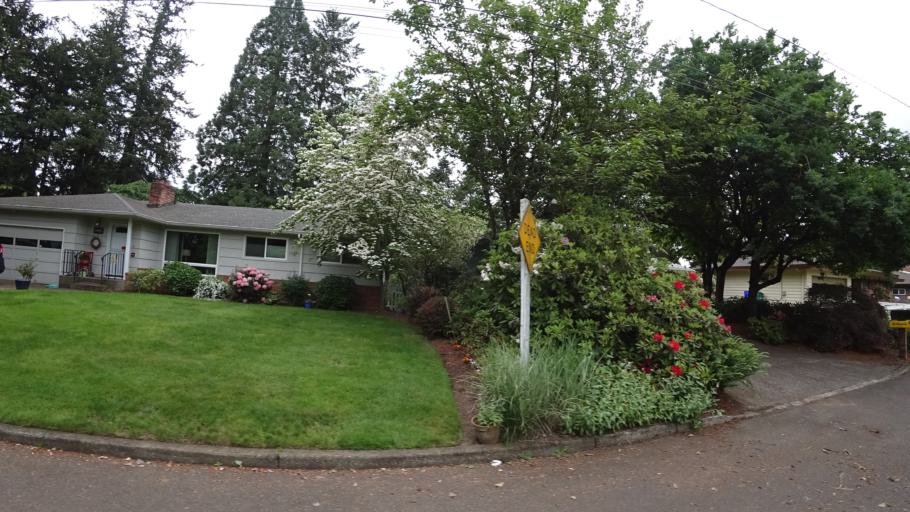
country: US
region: Oregon
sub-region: Multnomah County
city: Lents
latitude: 45.5071
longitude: -122.5454
